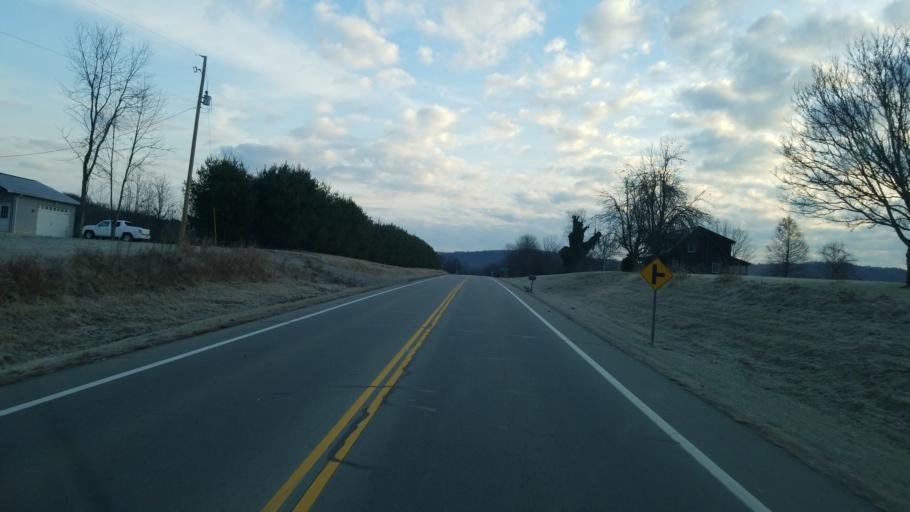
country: US
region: Ohio
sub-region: Ross County
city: North Fork Village
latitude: 39.3102
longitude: -83.1244
